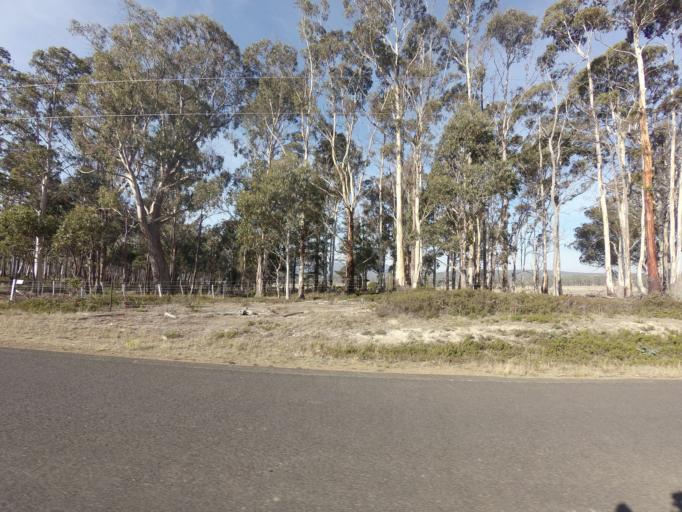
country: AU
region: Tasmania
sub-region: Sorell
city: Sorell
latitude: -42.4677
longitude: 147.4612
